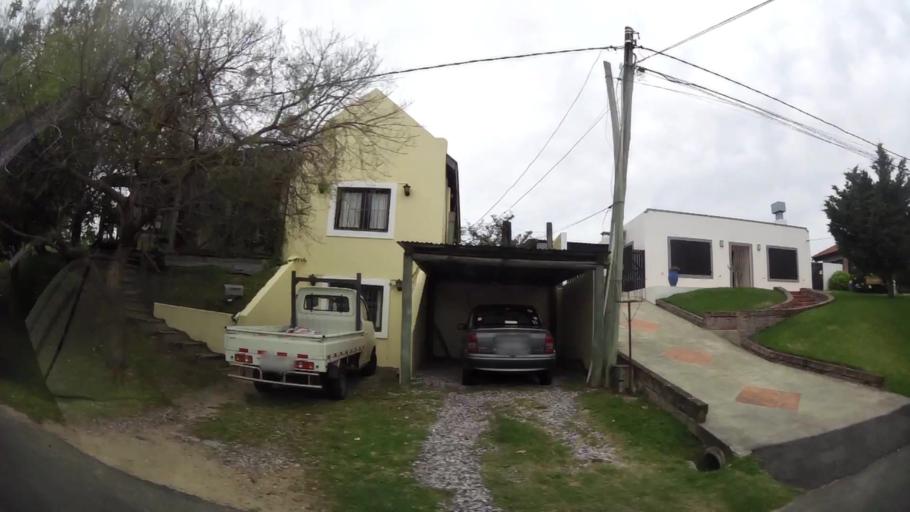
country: UY
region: Maldonado
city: Maldonado
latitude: -34.9054
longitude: -54.9744
